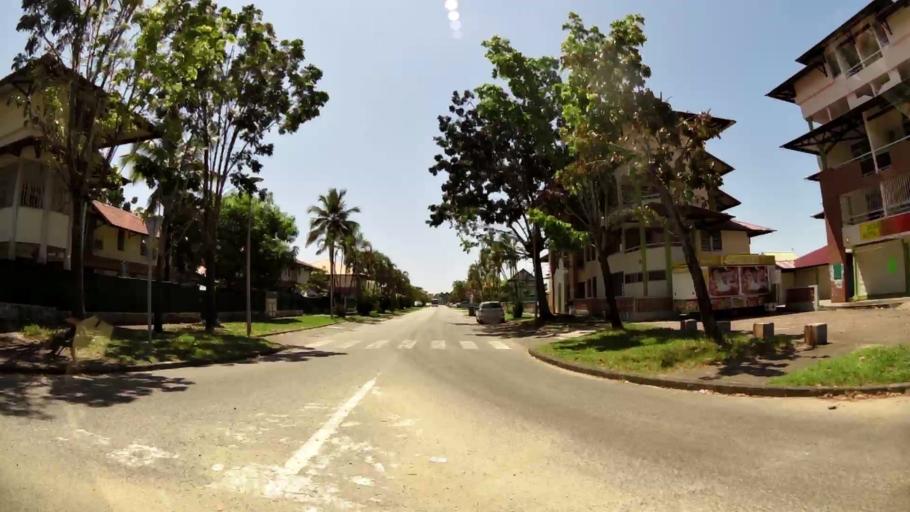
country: GF
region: Guyane
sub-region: Guyane
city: Kourou
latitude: 5.1742
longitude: -52.6484
